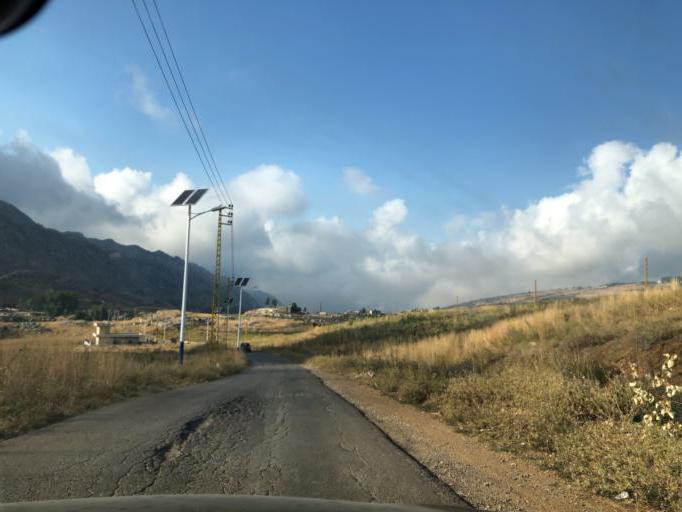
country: LB
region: Liban-Nord
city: Amioun
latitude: 34.1414
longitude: 35.8592
